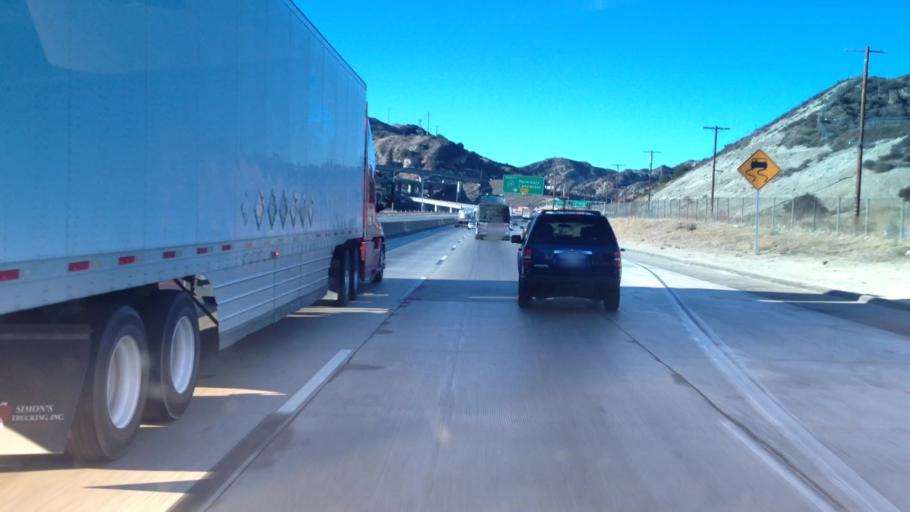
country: US
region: California
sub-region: Los Angeles County
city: Santa Clarita
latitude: 34.3283
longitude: -118.5028
